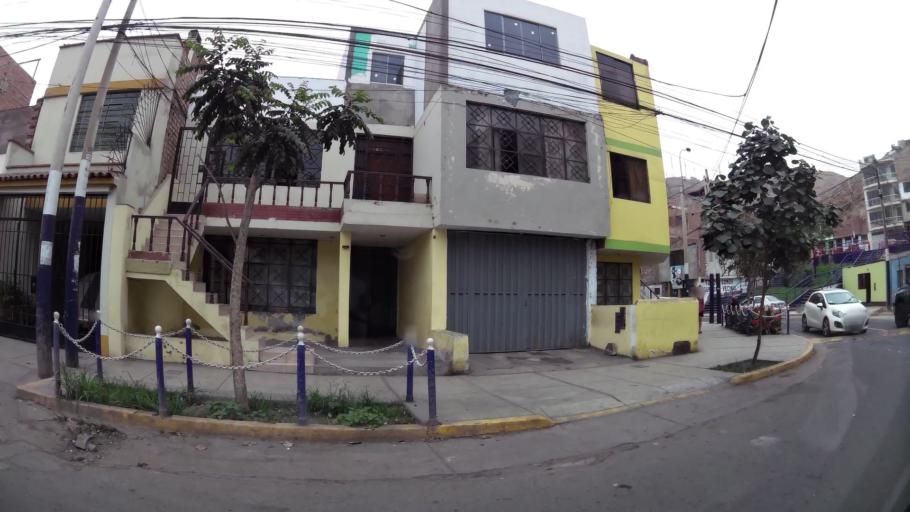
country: PE
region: Lima
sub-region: Lima
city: Surco
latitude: -12.1734
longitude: -77.0255
